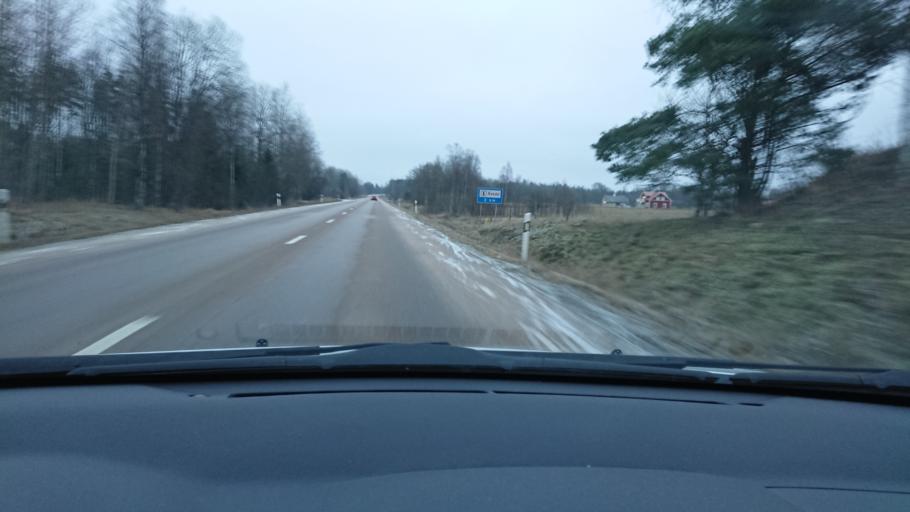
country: SE
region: Kronoberg
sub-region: Uppvidinge Kommun
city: Aseda
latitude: 57.1392
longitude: 15.2850
